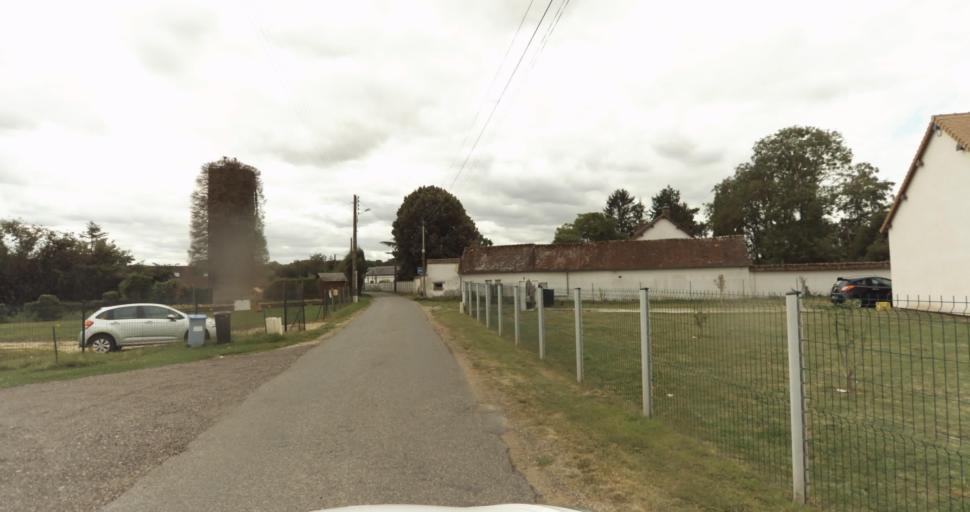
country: FR
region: Centre
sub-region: Departement d'Eure-et-Loir
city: Saint-Lubin-des-Joncherets
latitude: 48.8379
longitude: 1.2432
